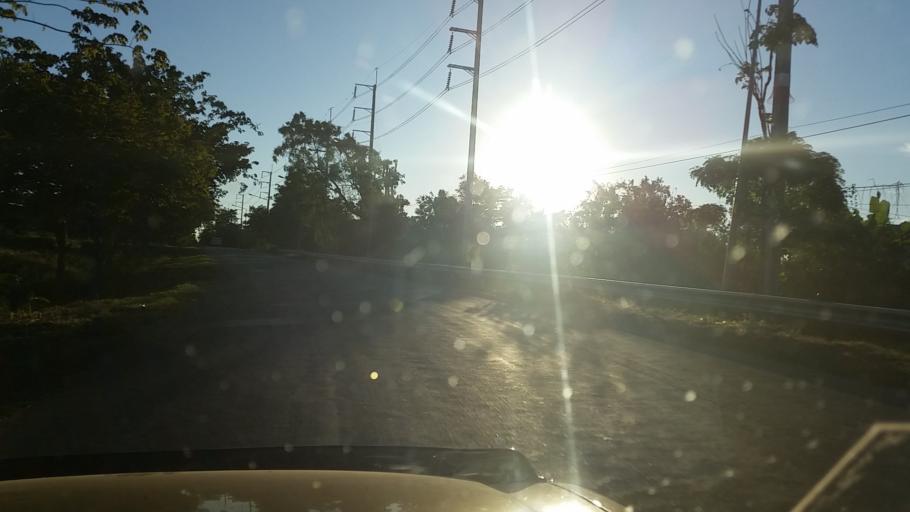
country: TH
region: Chaiyaphum
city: Sap Yai
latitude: 15.6588
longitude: 101.6462
